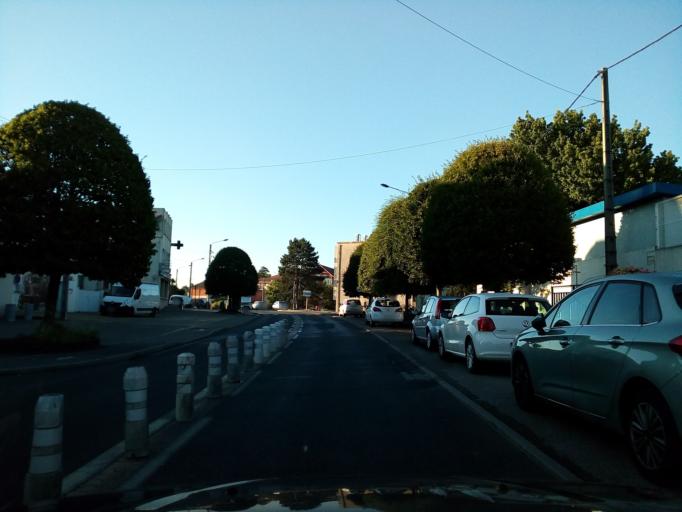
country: FR
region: Rhone-Alpes
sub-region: Departement de l'Isere
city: La Verpilliere
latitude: 45.6345
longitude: 5.1452
